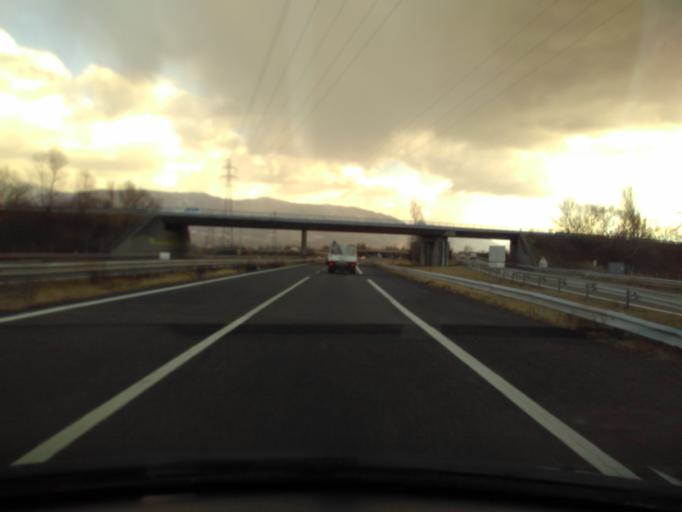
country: FR
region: Rhone-Alpes
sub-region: Departement de la Savoie
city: Les Marches
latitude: 45.4905
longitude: 6.0232
